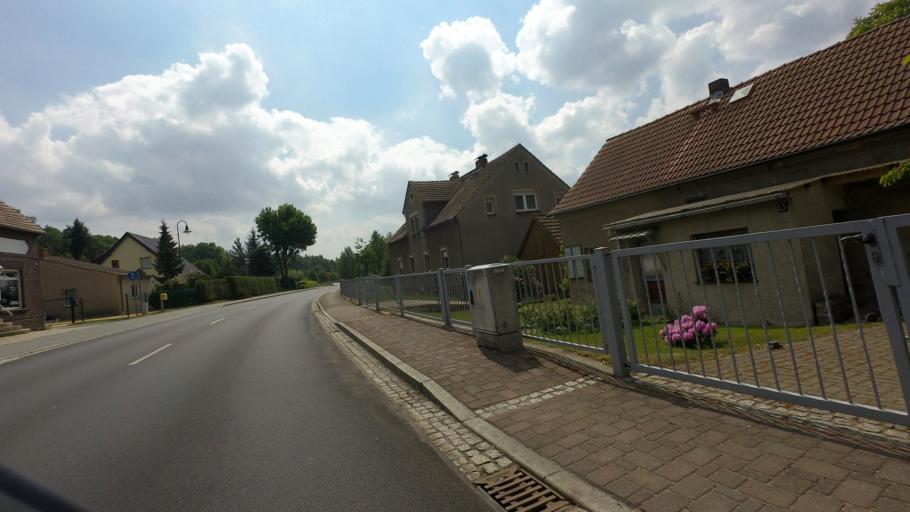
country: DE
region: Saxony
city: Rietschen
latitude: 51.3568
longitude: 14.8028
